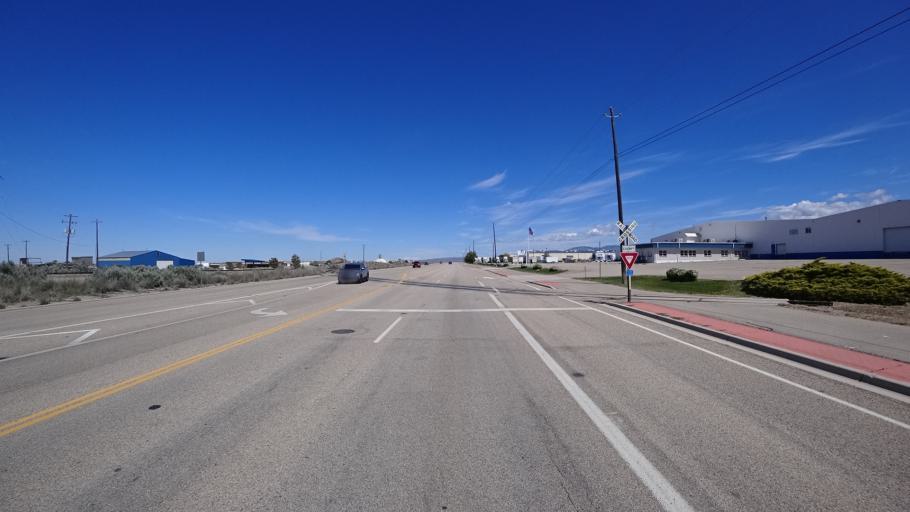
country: US
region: Idaho
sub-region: Ada County
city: Boise
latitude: 43.5509
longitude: -116.1605
